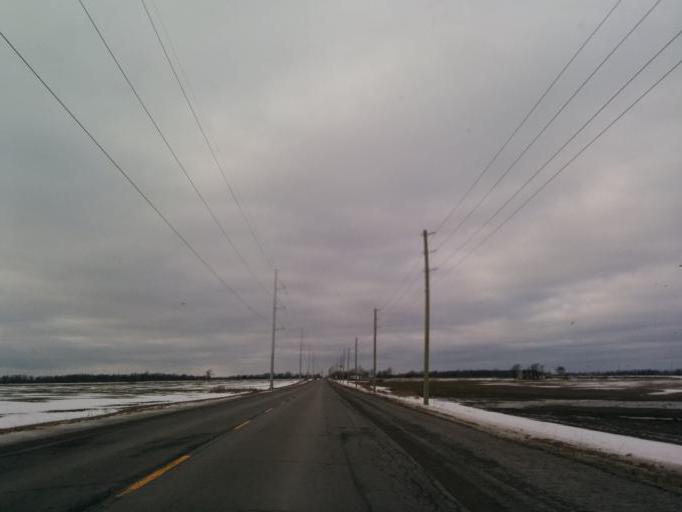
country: CA
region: Ontario
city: Ancaster
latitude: 42.9291
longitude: -79.9601
